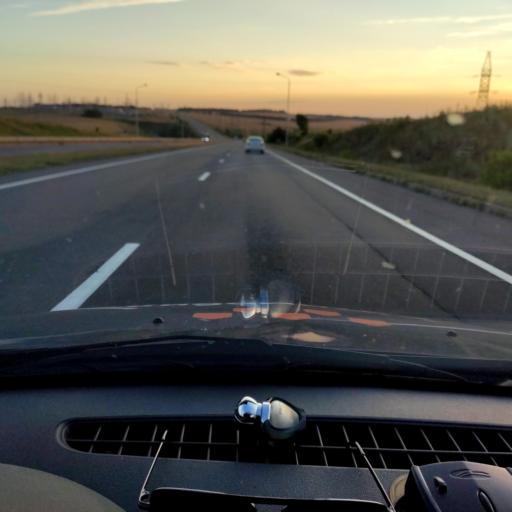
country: RU
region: Belgorod
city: Gubkin
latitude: 51.3195
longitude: 37.6604
